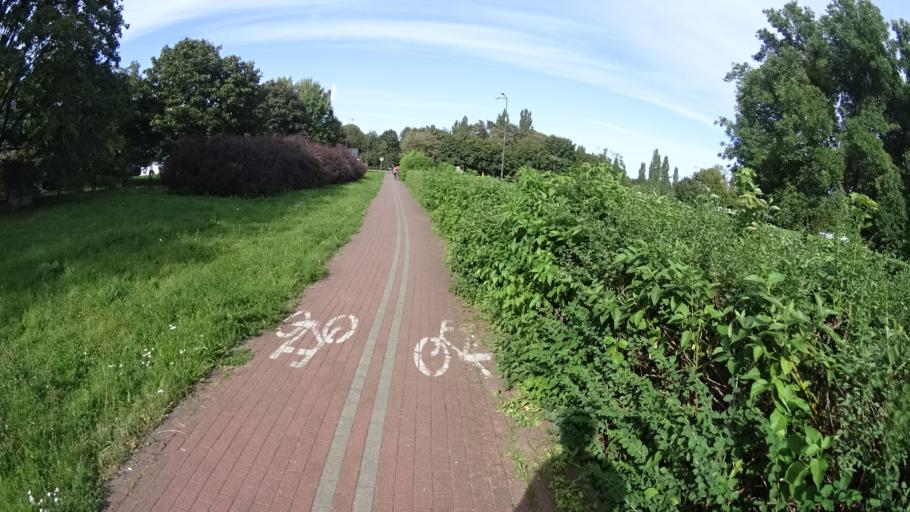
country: PL
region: Masovian Voivodeship
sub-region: Warszawa
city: Wola
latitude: 52.2375
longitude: 20.9504
